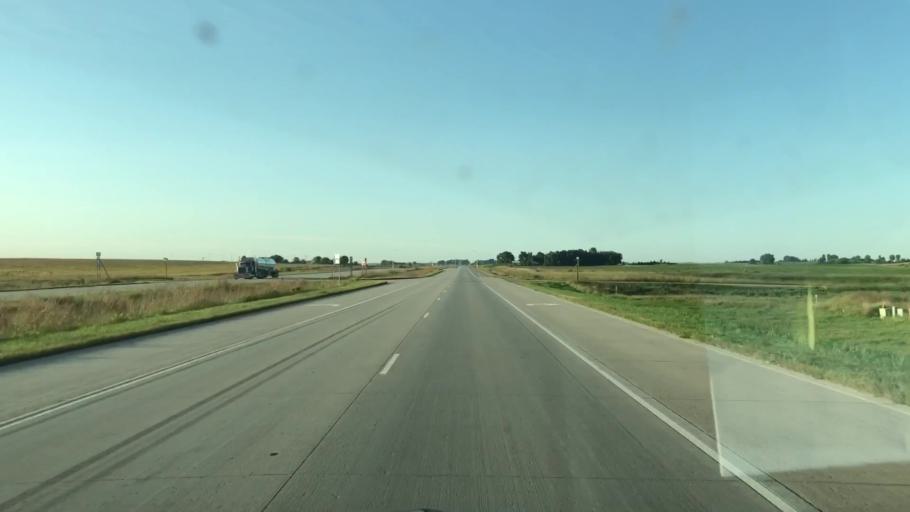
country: US
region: Minnesota
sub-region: Nobles County
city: Worthington
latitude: 43.5735
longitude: -95.6536
